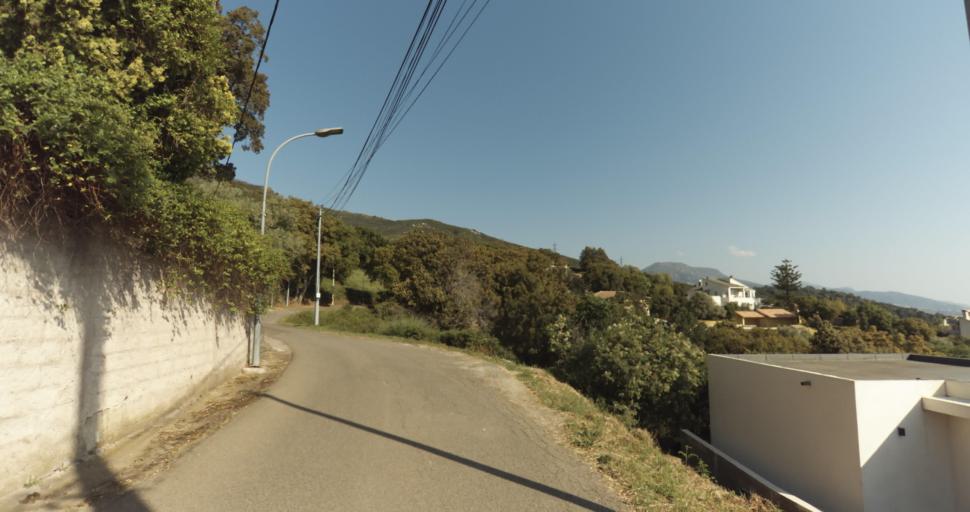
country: FR
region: Corsica
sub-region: Departement de la Haute-Corse
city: Biguglia
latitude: 42.6301
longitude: 9.4185
